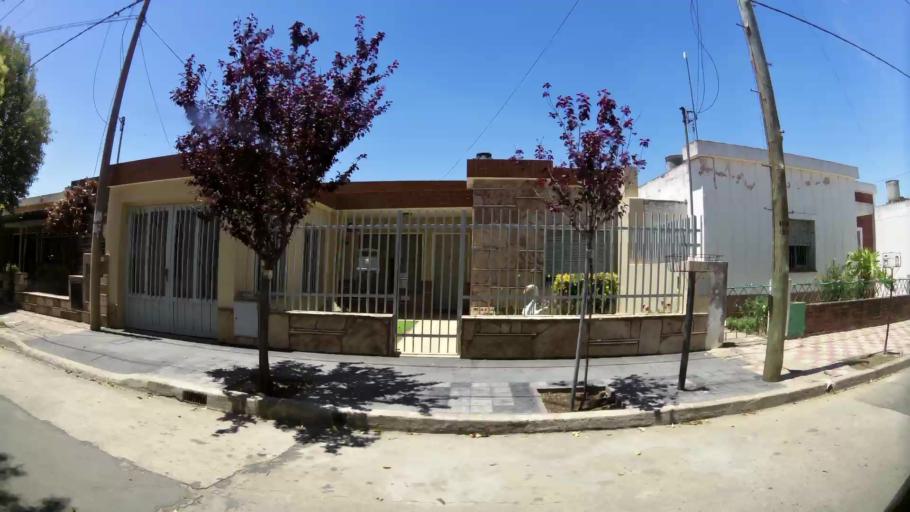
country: AR
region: Cordoba
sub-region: Departamento de Capital
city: Cordoba
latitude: -31.3839
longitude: -64.1311
